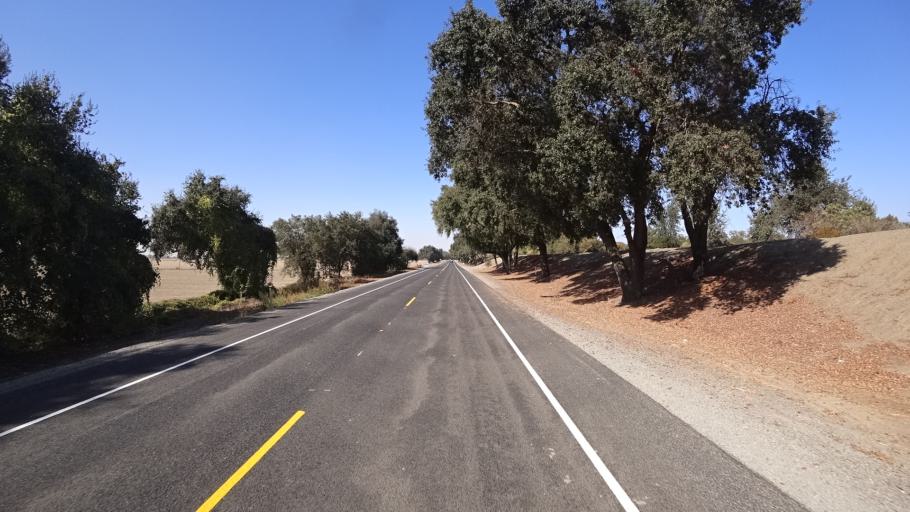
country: US
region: California
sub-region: Yolo County
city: West Sacramento
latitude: 38.6667
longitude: -121.6202
